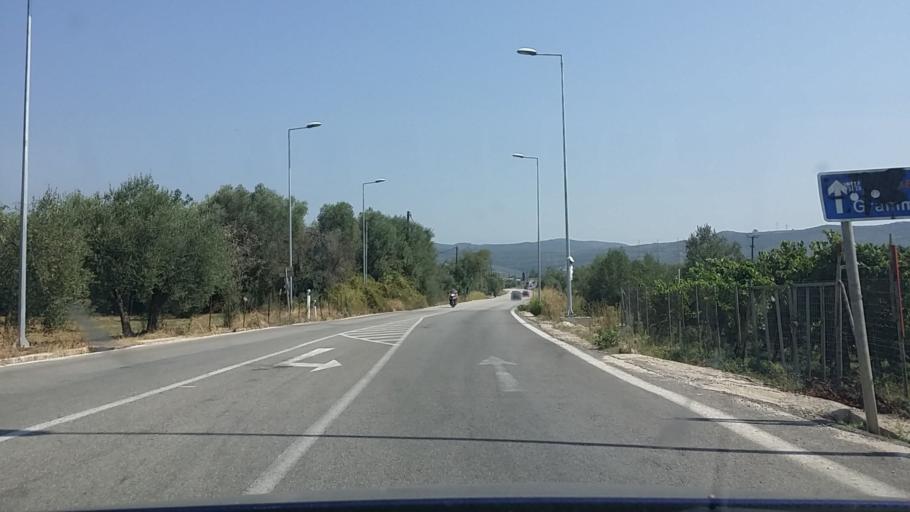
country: GR
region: Epirus
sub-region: Nomos Artas
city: Grammenitsa
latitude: 39.1737
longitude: 20.9703
